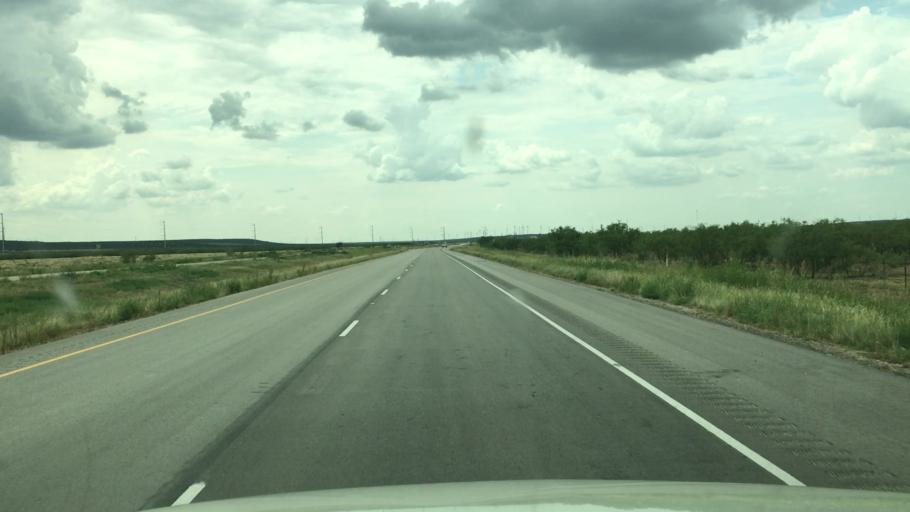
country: US
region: Texas
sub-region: Sterling County
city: Sterling City
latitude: 31.9625
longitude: -101.2186
